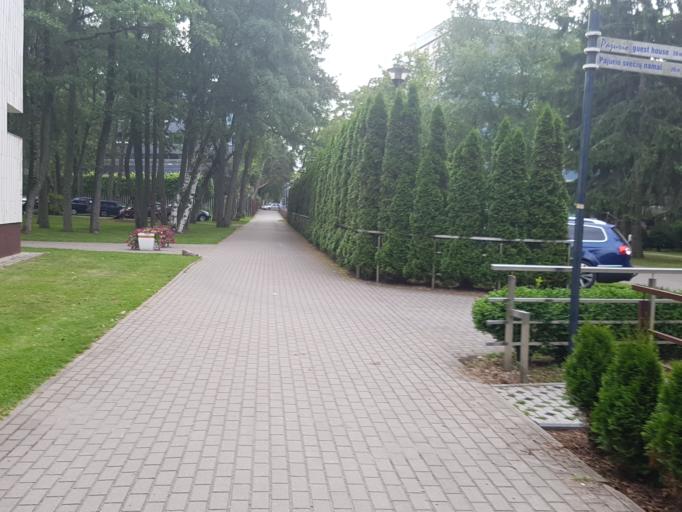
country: LT
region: Klaipedos apskritis
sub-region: Klaipeda
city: Palanga
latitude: 55.9138
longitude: 21.0534
